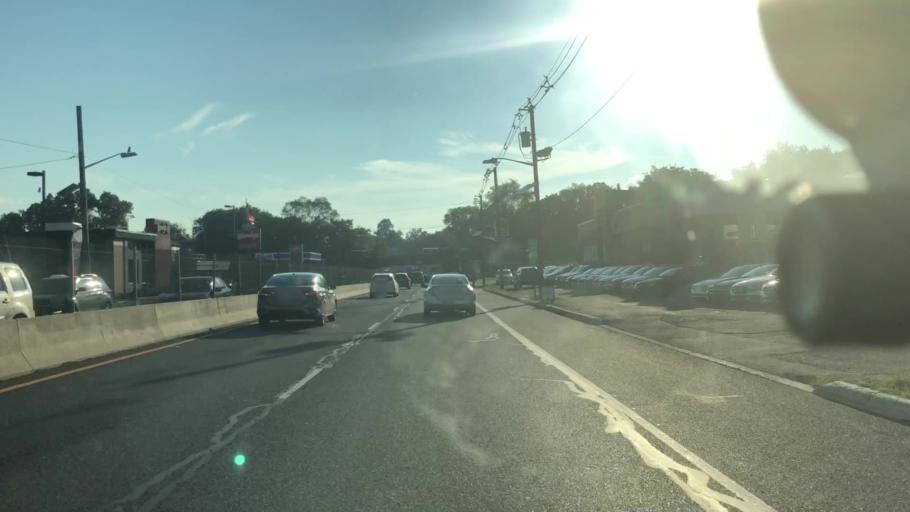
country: US
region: New Jersey
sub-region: Union County
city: Hillside
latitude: 40.6993
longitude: -74.2366
